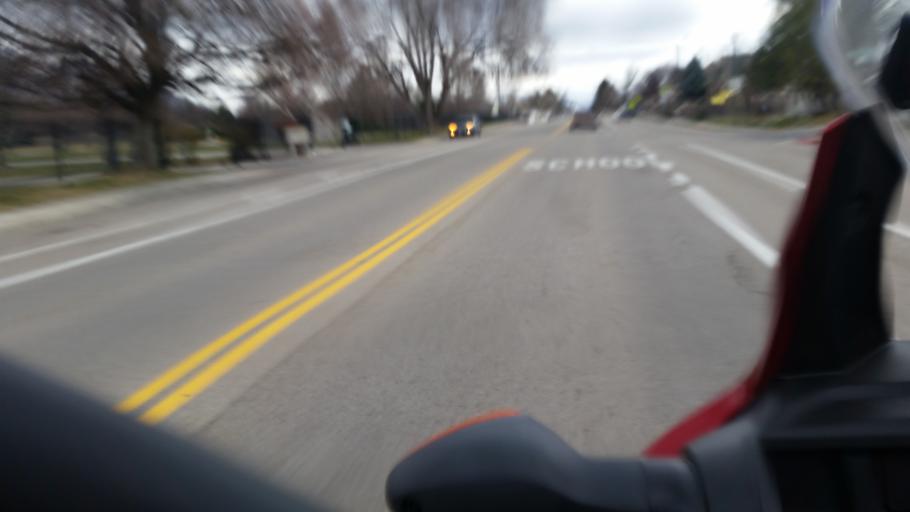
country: US
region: Utah
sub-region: Utah County
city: Orem
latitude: 40.3159
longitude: -111.6863
